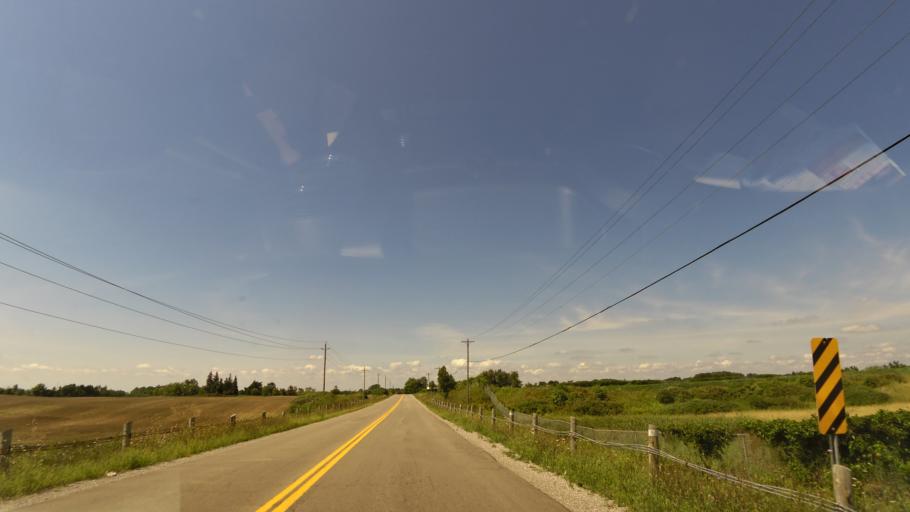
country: CA
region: Ontario
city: Ancaster
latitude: 43.1625
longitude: -79.9415
